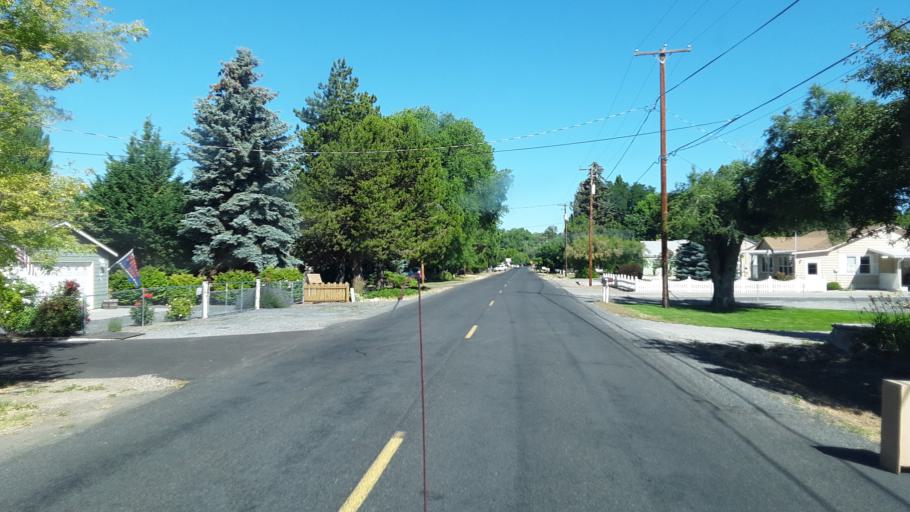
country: US
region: Oregon
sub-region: Klamath County
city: Altamont
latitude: 42.1965
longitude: -121.7270
